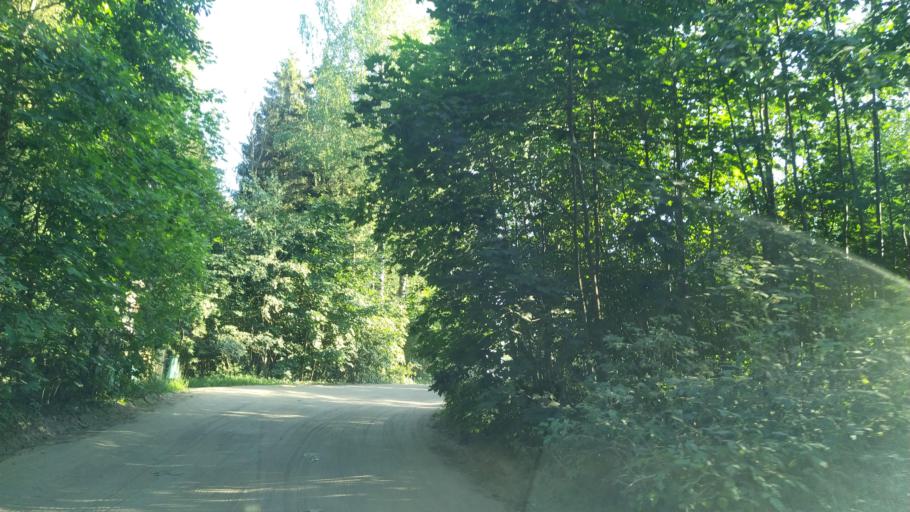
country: RU
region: Leningrad
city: Koltushi
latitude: 59.9058
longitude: 30.7355
